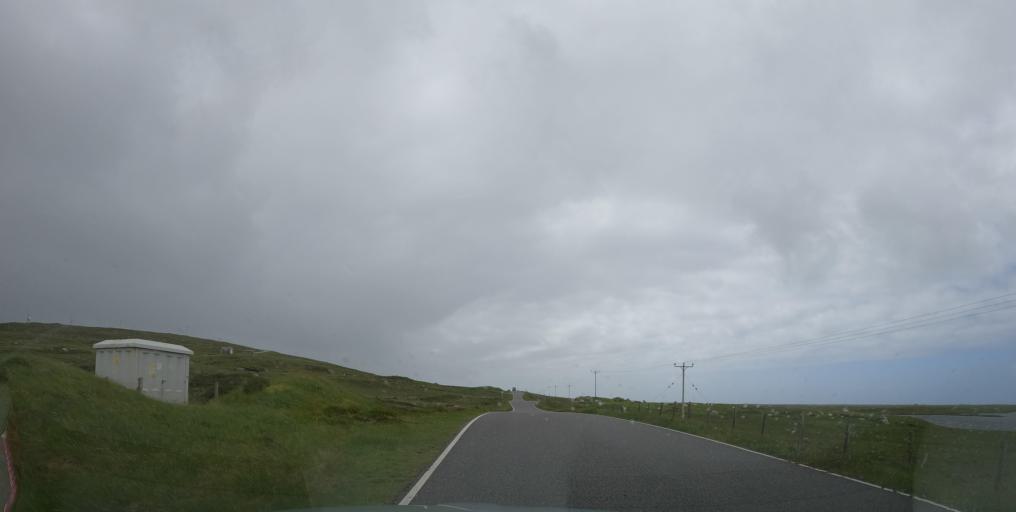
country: GB
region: Scotland
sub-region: Eilean Siar
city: Benbecula
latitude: 57.3477
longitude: -7.3601
